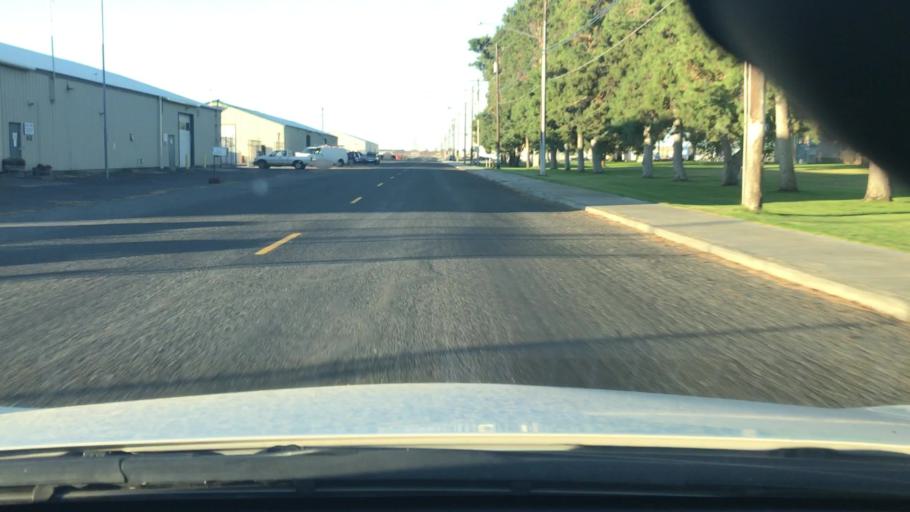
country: US
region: Washington
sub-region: Grant County
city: Moses Lake North
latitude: 47.1858
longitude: -119.3166
